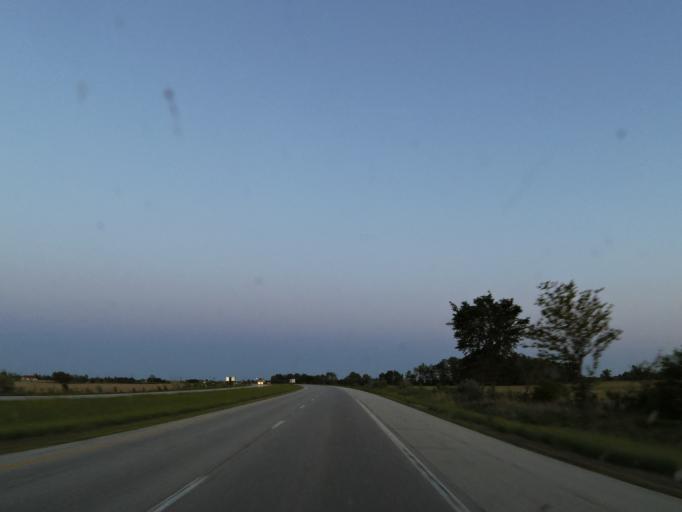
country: US
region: Indiana
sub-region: Boone County
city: Thorntown
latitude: 39.9483
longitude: -86.6323
